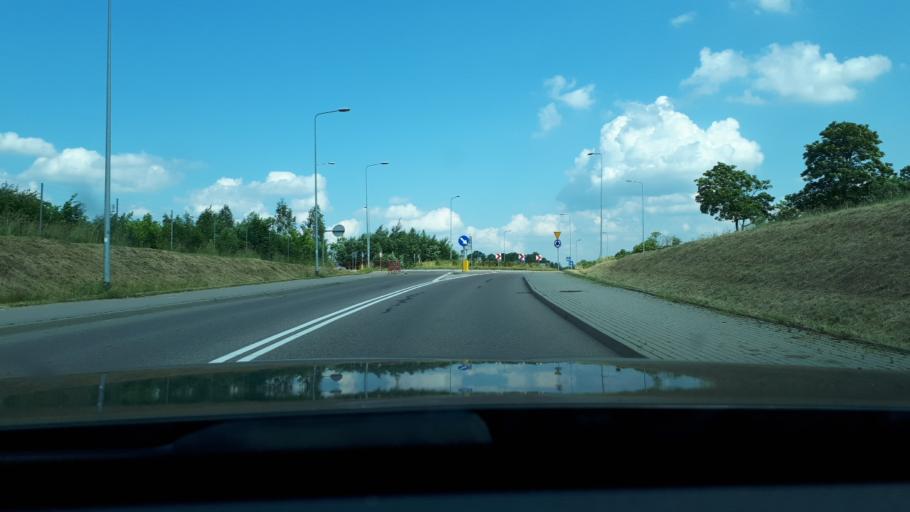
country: PL
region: Podlasie
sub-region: Powiat bialostocki
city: Choroszcz
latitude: 53.1604
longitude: 22.9980
